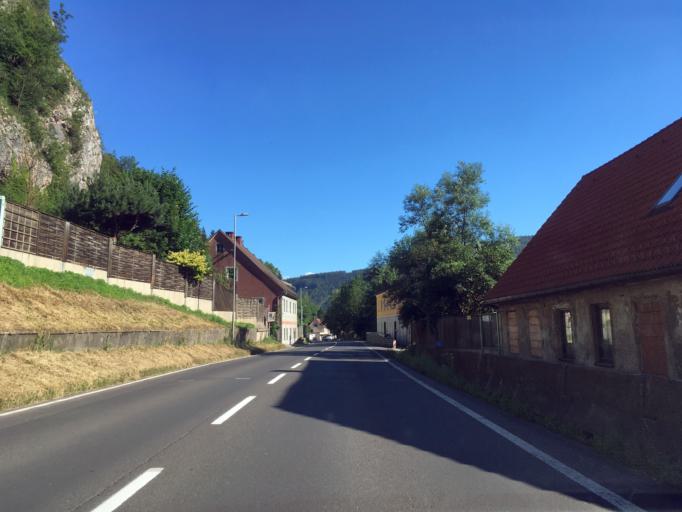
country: AT
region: Styria
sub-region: Politischer Bezirk Leoben
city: Sankt Peter-Freienstein
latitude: 47.4022
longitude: 15.0323
